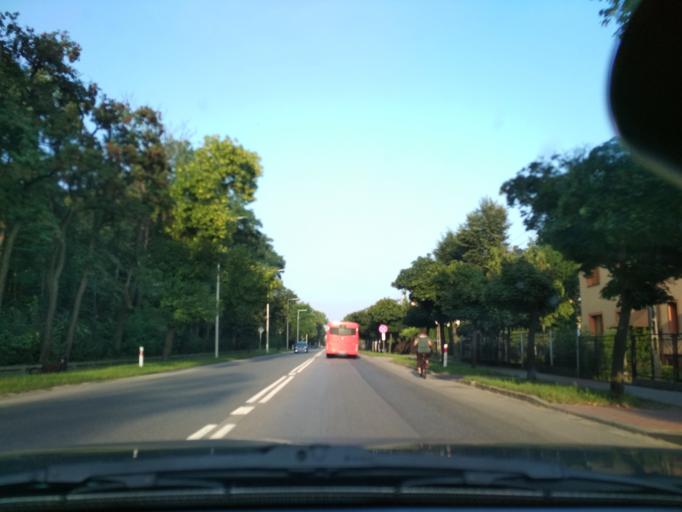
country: PL
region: Silesian Voivodeship
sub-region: Powiat zawiercianski
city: Zawiercie
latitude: 50.4785
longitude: 19.4483
